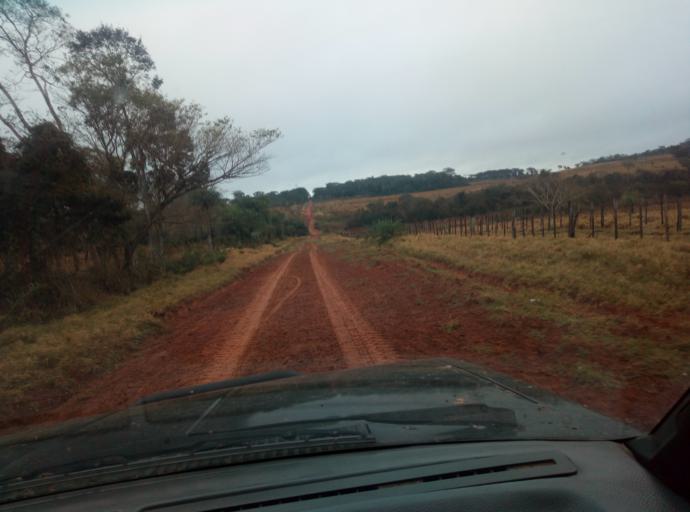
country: PY
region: Caaguazu
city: Carayao
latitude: -25.1930
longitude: -56.3329
